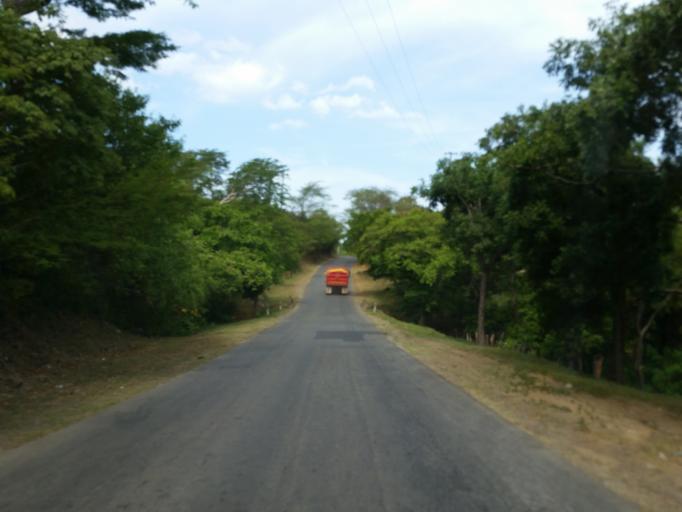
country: NI
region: Managua
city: Masachapa
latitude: 11.8152
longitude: -86.4801
